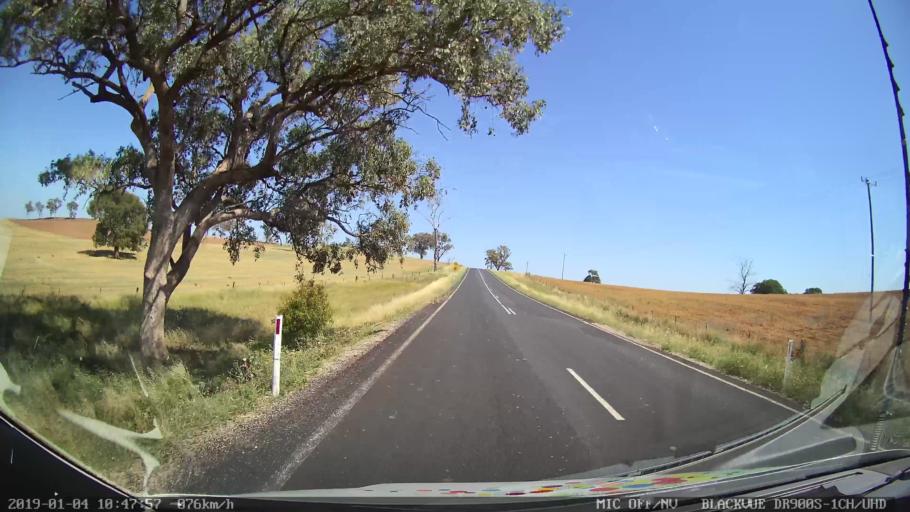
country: AU
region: New South Wales
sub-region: Cabonne
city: Molong
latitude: -33.2649
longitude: 148.7162
